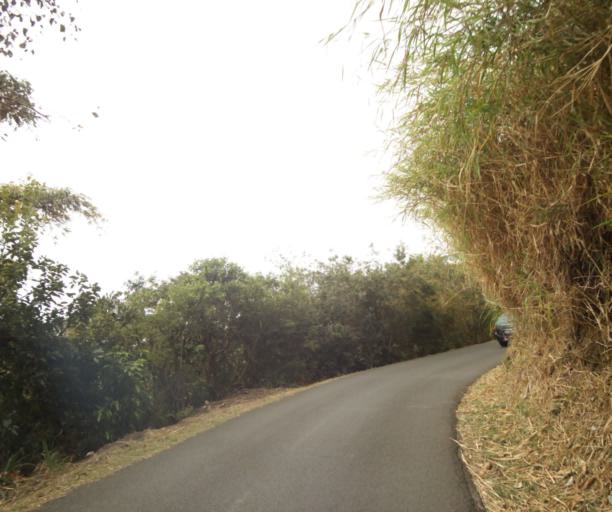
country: RE
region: Reunion
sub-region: Reunion
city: Saint-Paul
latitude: -21.0266
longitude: 55.3049
